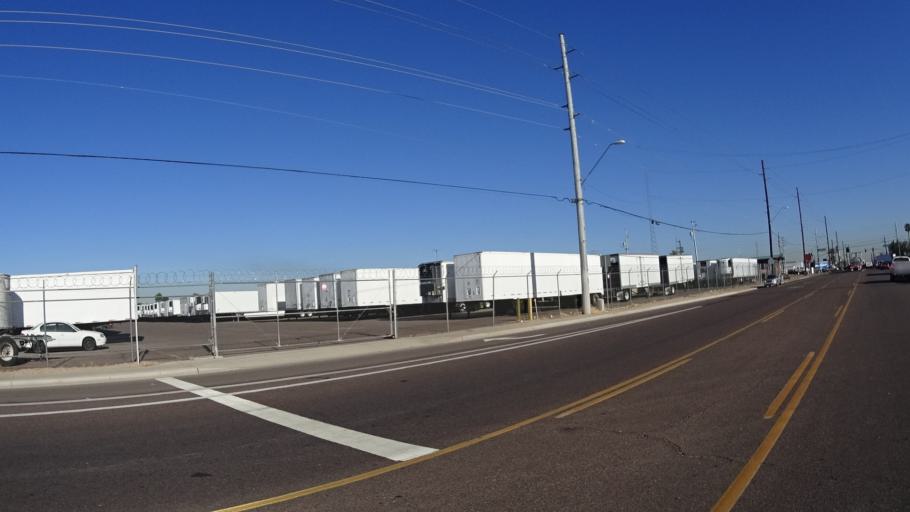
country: US
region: Arizona
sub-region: Maricopa County
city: Phoenix
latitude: 33.4351
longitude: -112.1172
